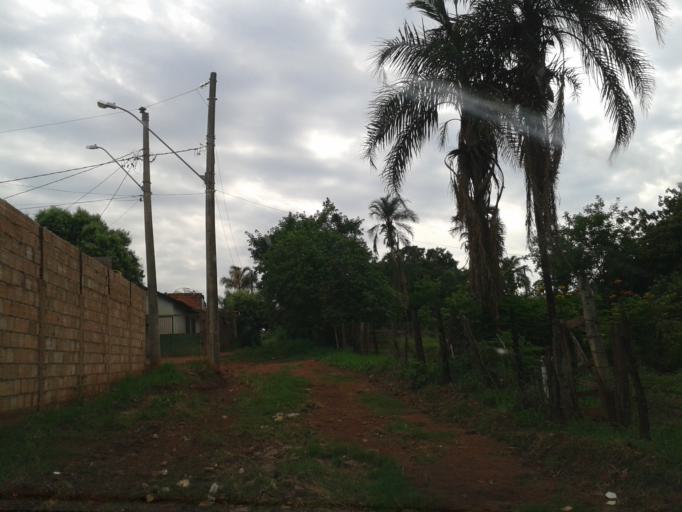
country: BR
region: Minas Gerais
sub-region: Ituiutaba
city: Ituiutaba
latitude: -18.9783
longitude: -49.4439
